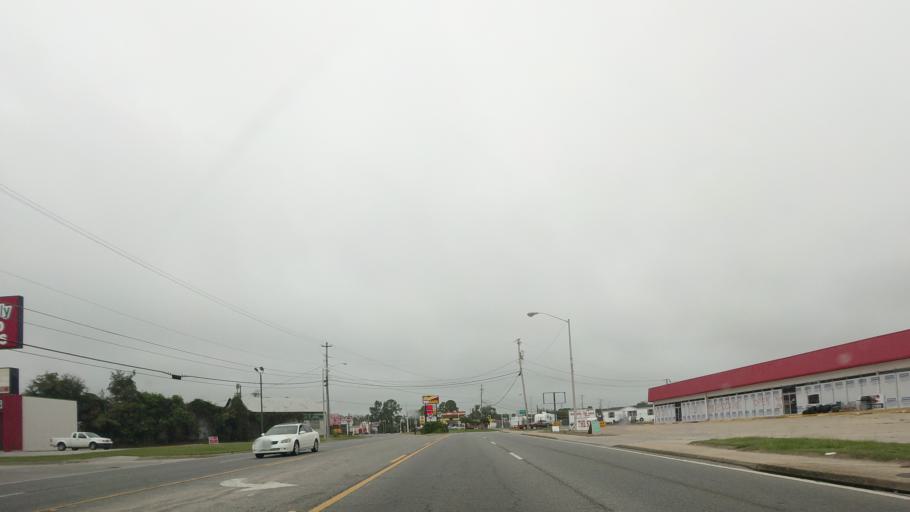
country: US
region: Georgia
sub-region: Ben Hill County
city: Fitzgerald
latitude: 31.7039
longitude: -83.2524
